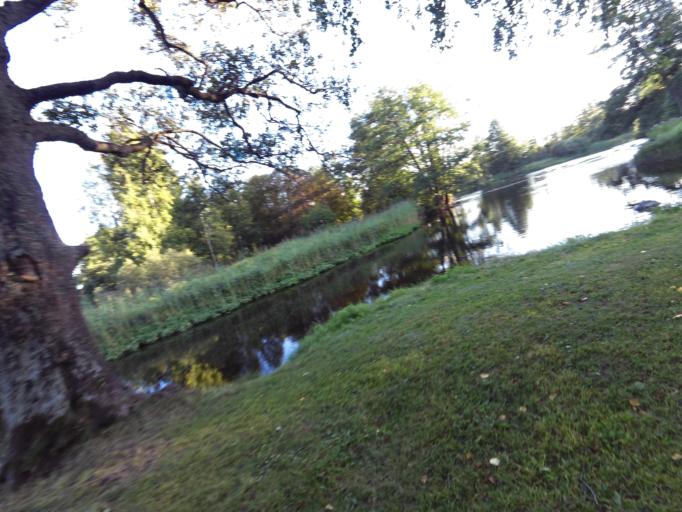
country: SE
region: Gaevleborg
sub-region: Gavle Kommun
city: Gavle
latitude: 60.7170
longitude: 17.1426
